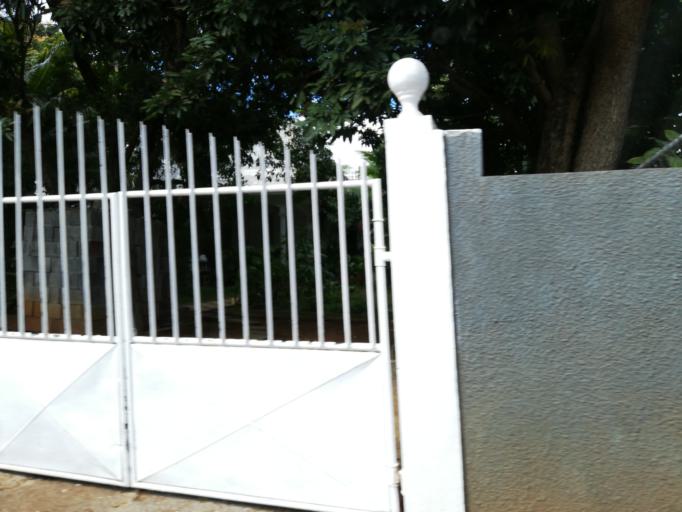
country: MU
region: Black River
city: Petite Riviere
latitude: -20.2177
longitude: 57.4635
